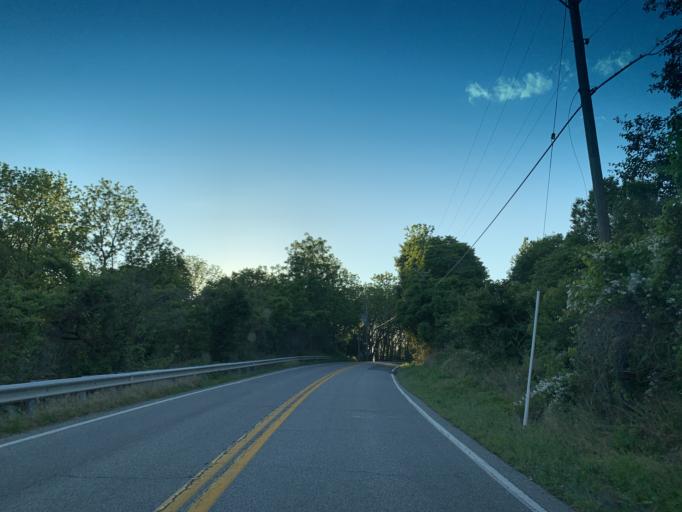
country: US
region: Maryland
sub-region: Cecil County
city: Elkton
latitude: 39.7146
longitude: -75.8755
